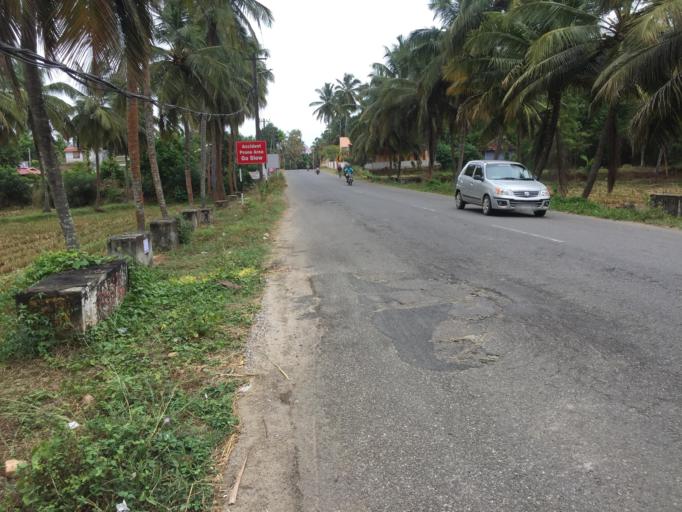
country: IN
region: Kerala
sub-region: Palakkad district
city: Chittur
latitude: 10.6839
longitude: 76.7138
